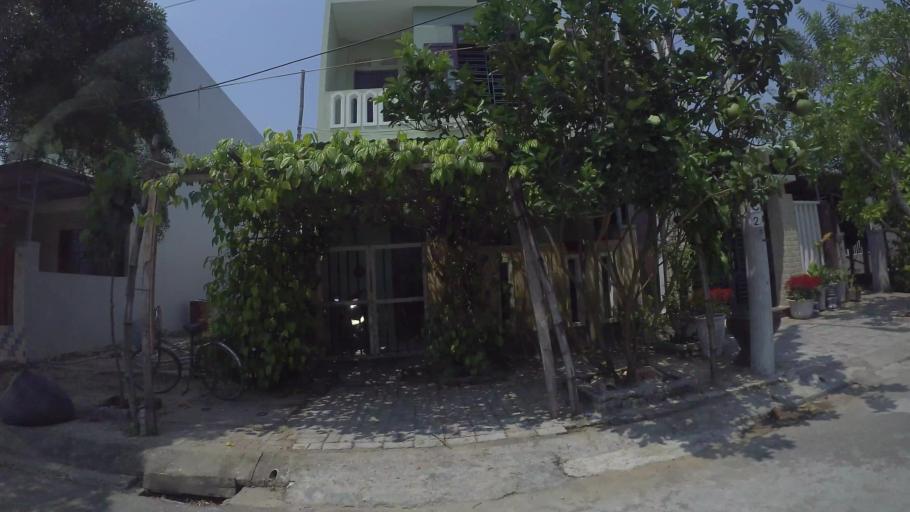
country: VN
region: Da Nang
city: Ngu Hanh Son
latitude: 15.9859
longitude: 108.2592
